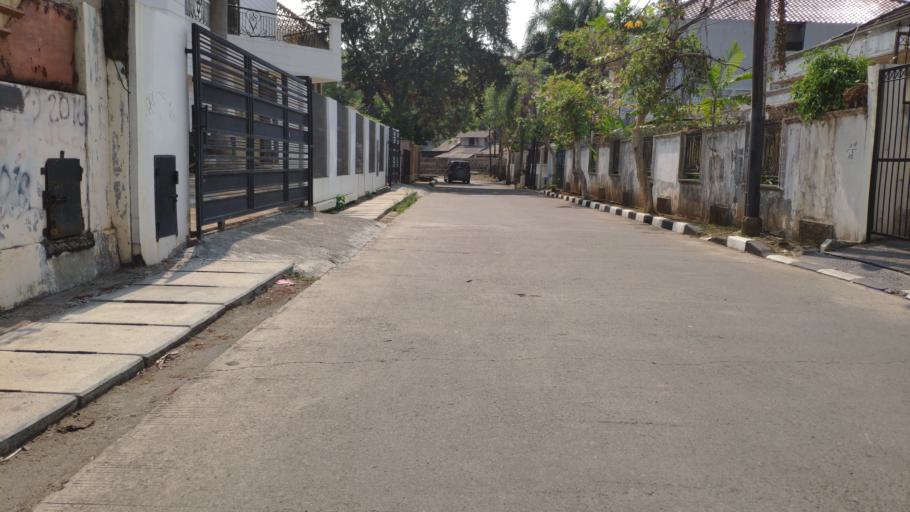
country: ID
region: Jakarta Raya
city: Jakarta
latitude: -6.2598
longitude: 106.8256
